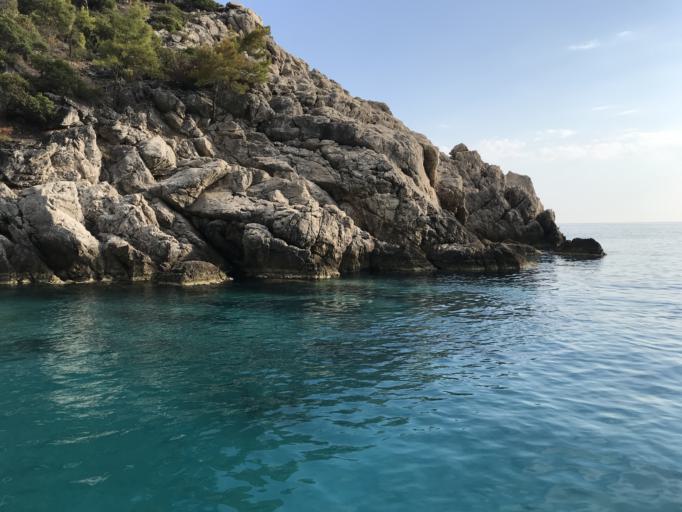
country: TR
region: Mugla
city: OEluedeniz
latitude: 36.4437
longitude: 29.1292
